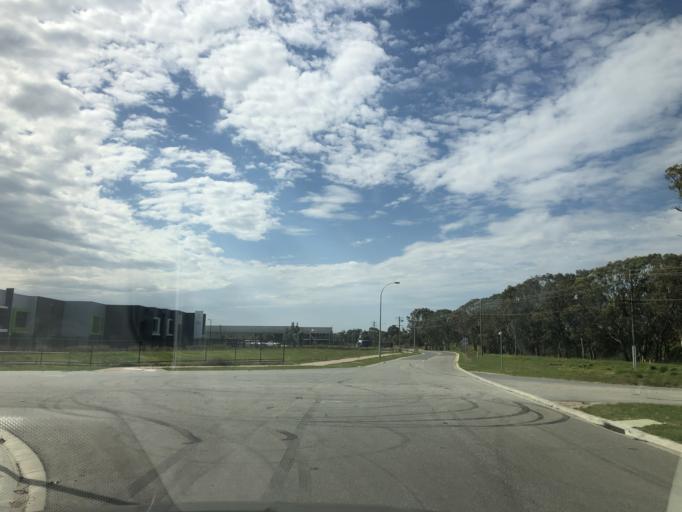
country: AU
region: Victoria
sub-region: Casey
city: Hampton Park
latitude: -38.0438
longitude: 145.2266
